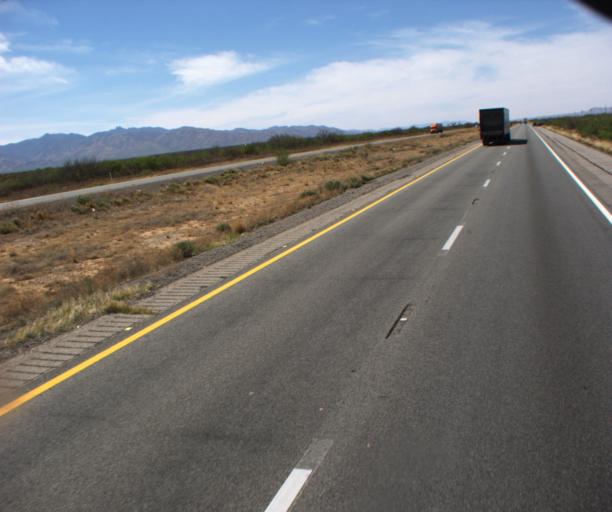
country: US
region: Arizona
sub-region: Cochise County
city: Willcox
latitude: 32.3024
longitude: -109.3753
